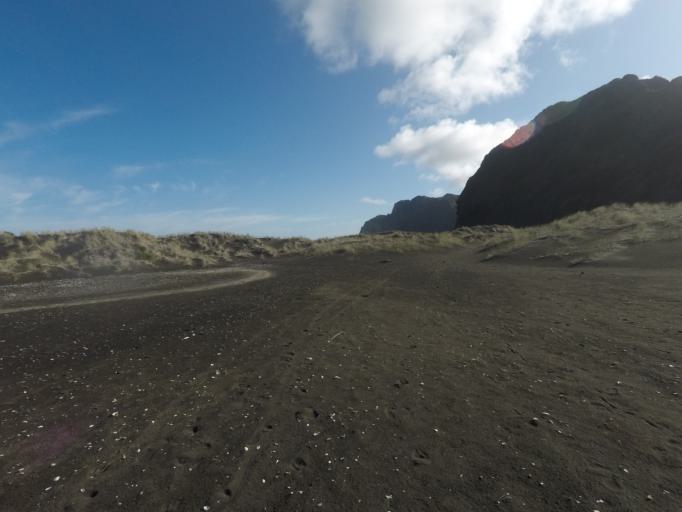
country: NZ
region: Auckland
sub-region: Auckland
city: Muriwai Beach
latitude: -36.9957
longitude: 174.4741
